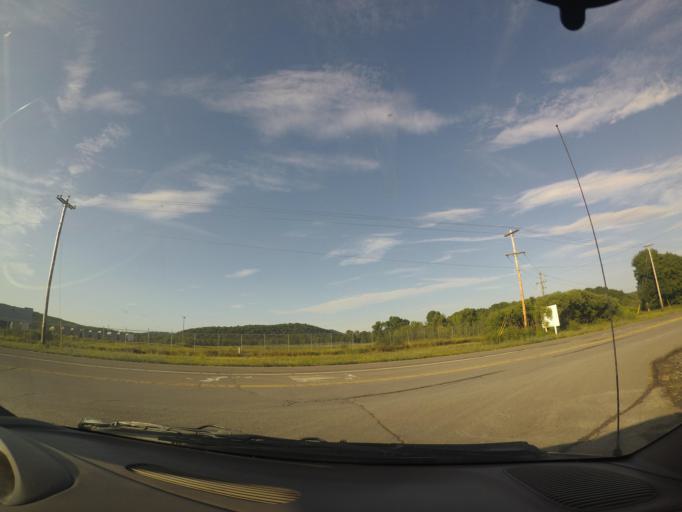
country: US
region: New York
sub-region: Tioga County
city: Owego
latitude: 42.0631
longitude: -76.3238
